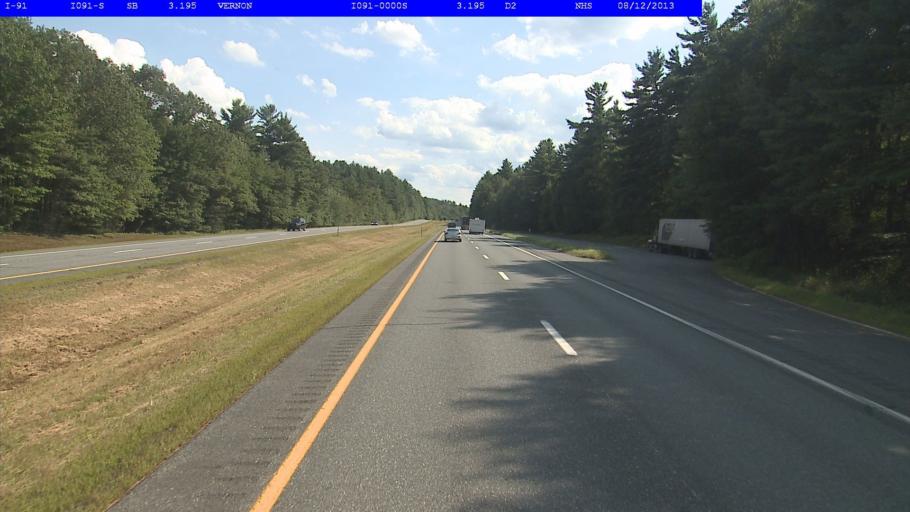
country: US
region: Vermont
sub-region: Windham County
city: Brattleboro
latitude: 42.7757
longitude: -72.5614
